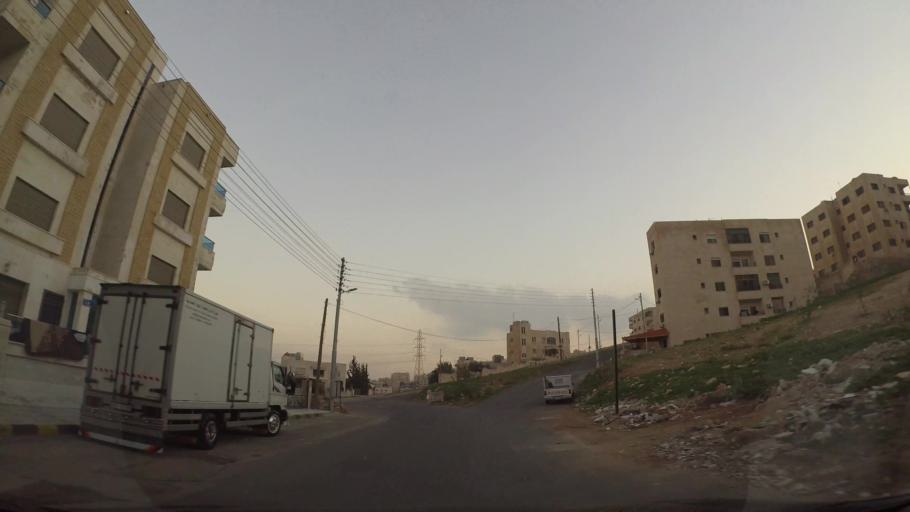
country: JO
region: Amman
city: Amman
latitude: 31.9900
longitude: 35.9715
